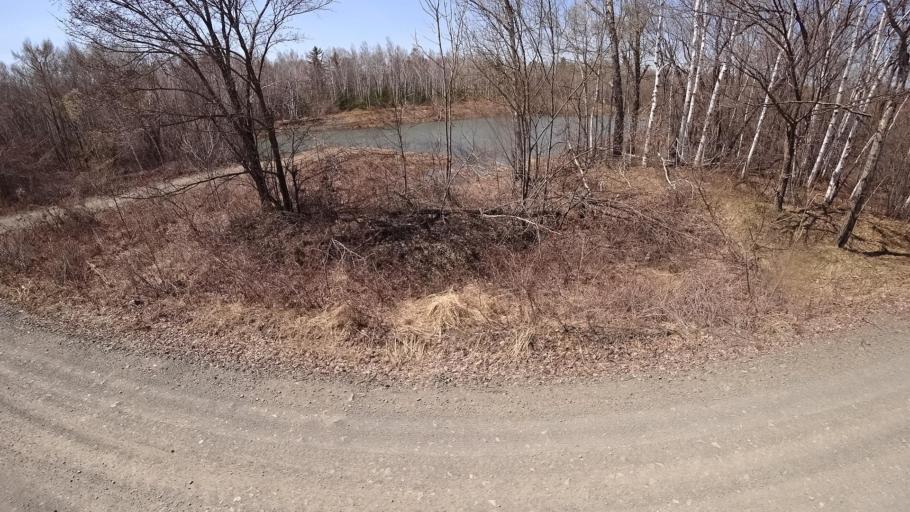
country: RU
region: Khabarovsk Krai
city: Khurba
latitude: 50.4113
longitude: 136.8436
